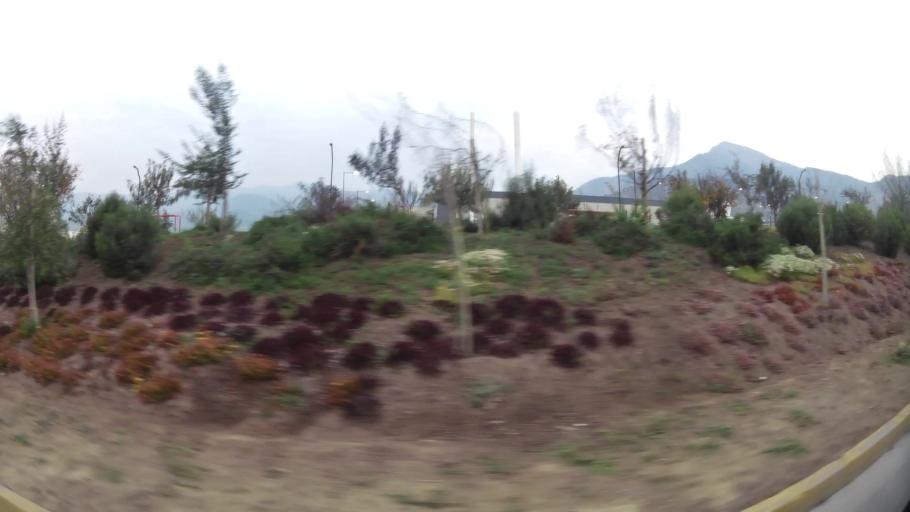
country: CL
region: Santiago Metropolitan
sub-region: Provincia de Chacabuco
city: Chicureo Abajo
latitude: -33.3209
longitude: -70.6469
